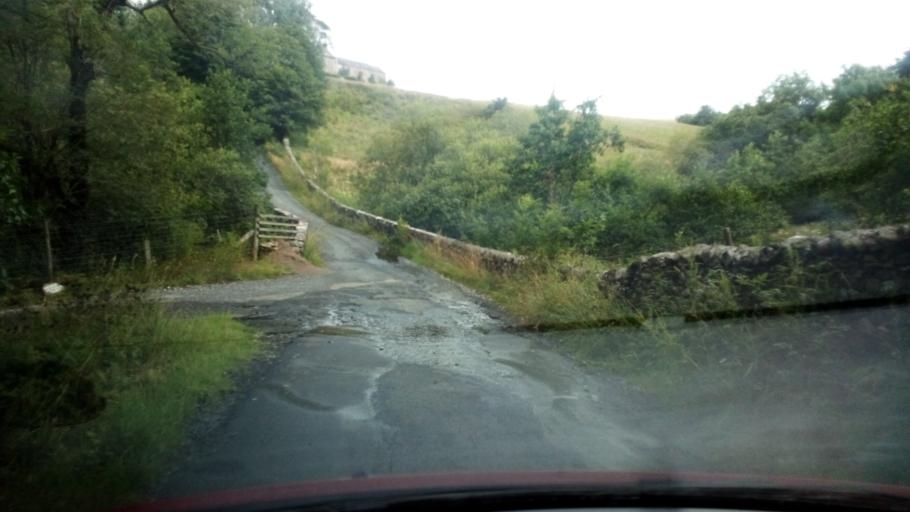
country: GB
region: England
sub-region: North Yorkshire
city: Settle
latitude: 54.0227
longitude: -2.4073
